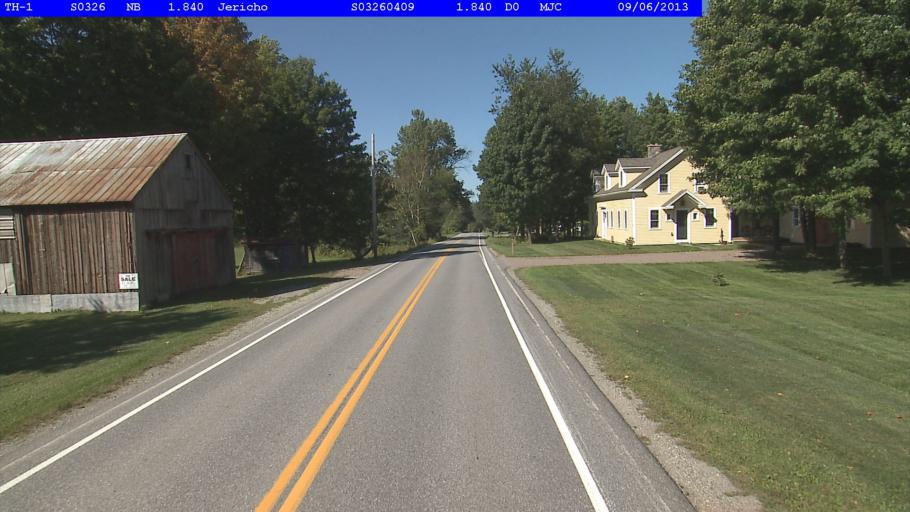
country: US
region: Vermont
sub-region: Chittenden County
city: Jericho
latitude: 44.5031
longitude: -72.9540
